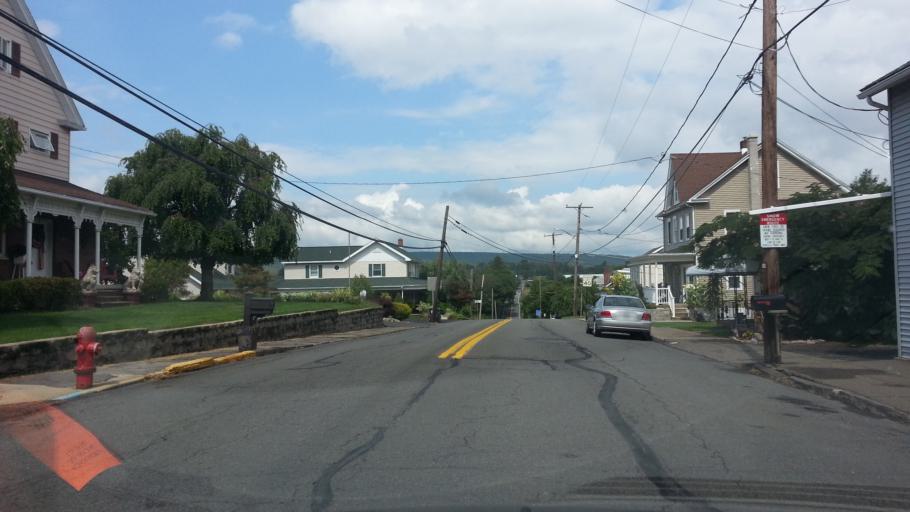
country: US
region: Pennsylvania
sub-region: Schuylkill County
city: Shenandoah Heights
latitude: 40.8604
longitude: -76.2314
